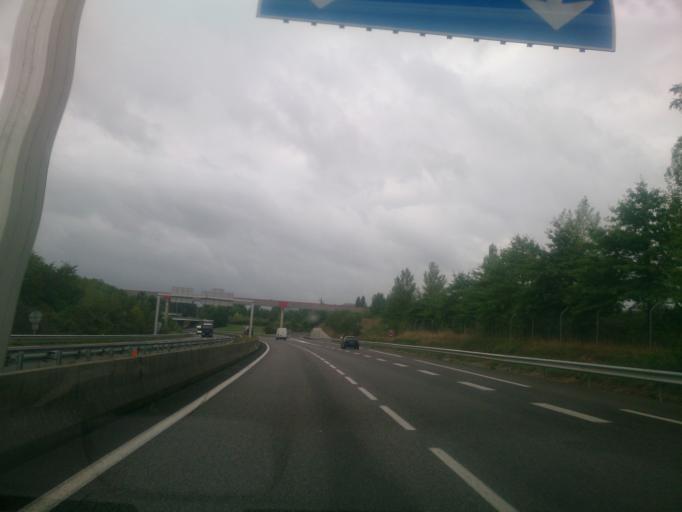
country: FR
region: Midi-Pyrenees
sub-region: Departement de la Haute-Garonne
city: Martres-Tolosane
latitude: 43.1892
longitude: 0.9824
